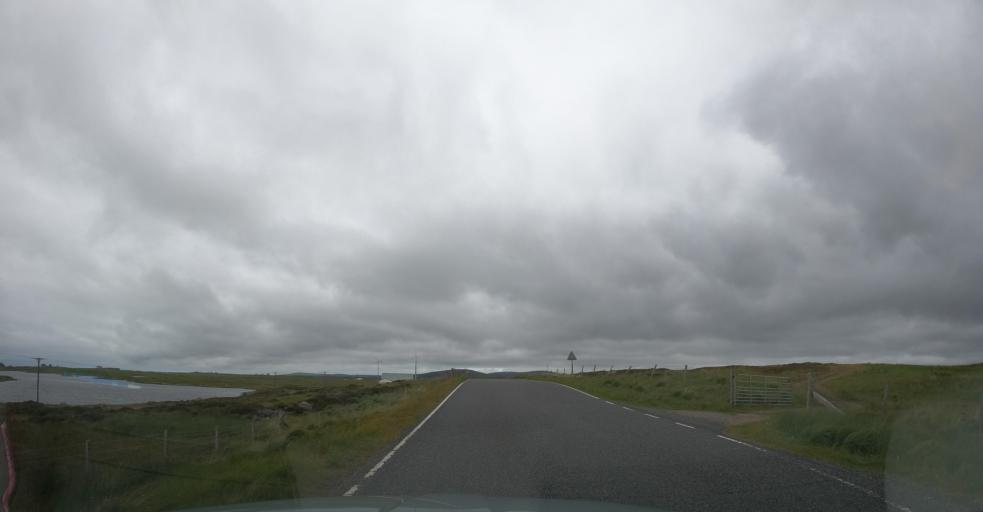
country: GB
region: Scotland
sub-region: Eilean Siar
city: Isle of North Uist
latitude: 57.5433
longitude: -7.3250
